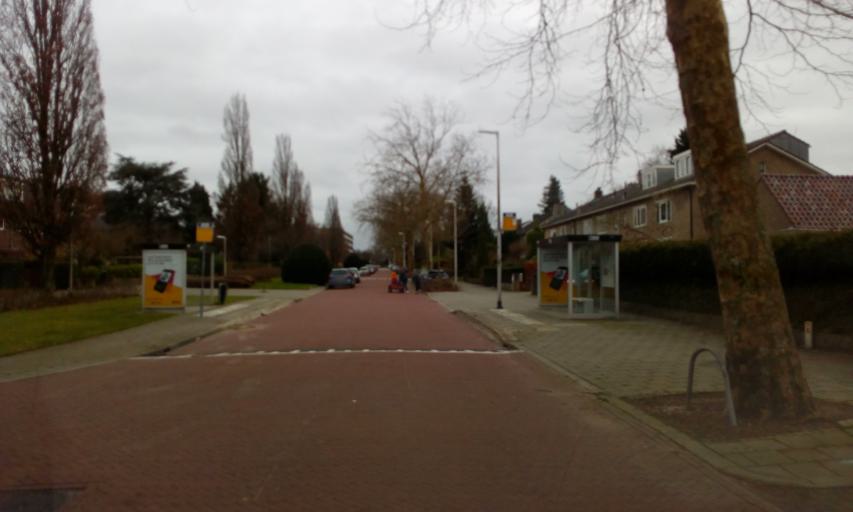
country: NL
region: North Holland
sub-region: Gemeente Bussum
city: Bussum
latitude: 52.2735
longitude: 5.1839
